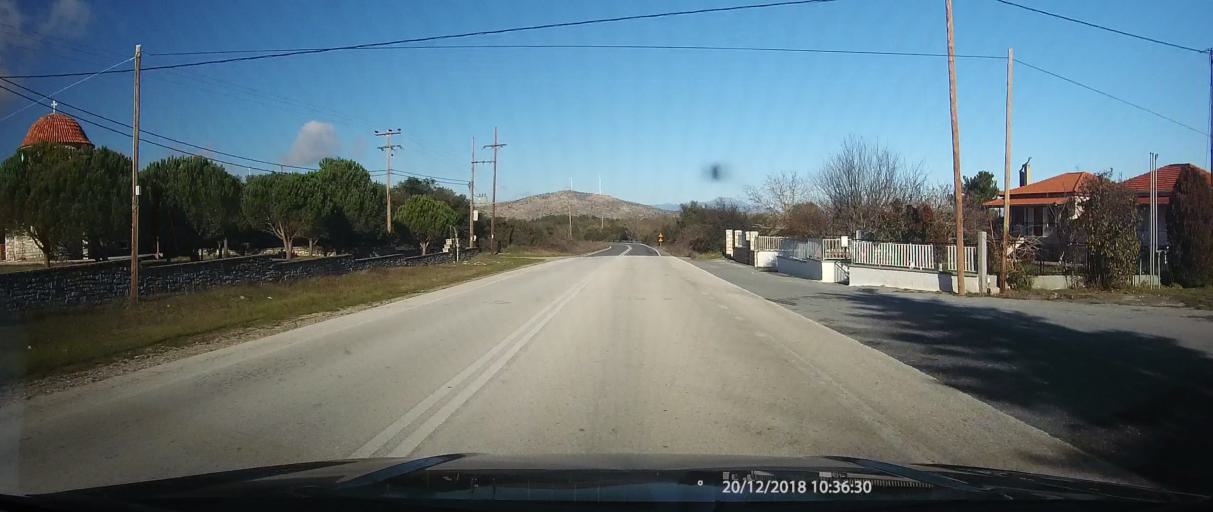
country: GR
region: Peloponnese
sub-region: Nomos Lakonias
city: Kariai
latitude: 37.3670
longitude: 22.4010
